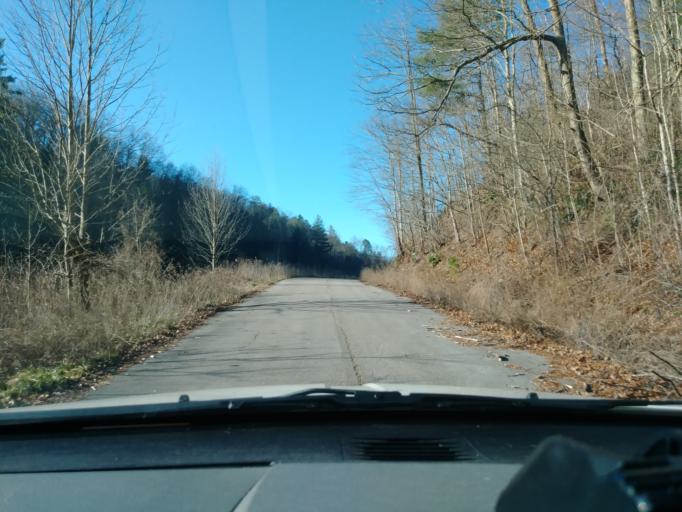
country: US
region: North Carolina
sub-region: Madison County
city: Marshall
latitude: 35.9115
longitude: -82.7897
